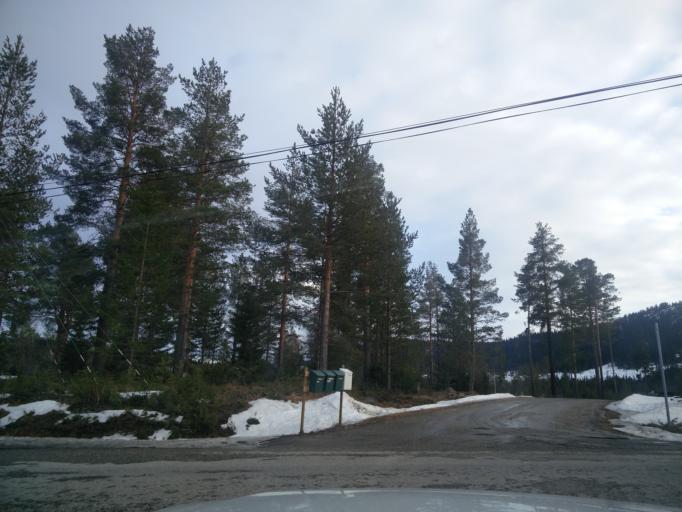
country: SE
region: Jaemtland
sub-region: Bergs Kommun
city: Hoverberg
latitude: 62.5048
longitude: 14.1894
